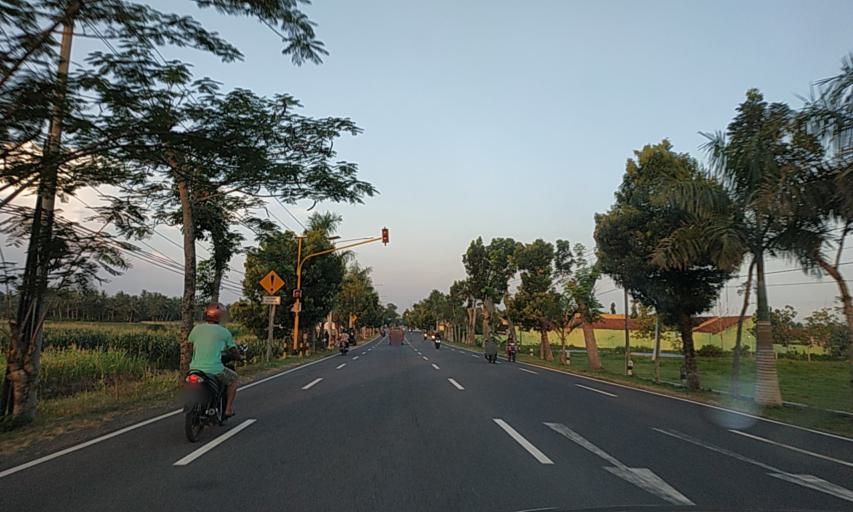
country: ID
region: Daerah Istimewa Yogyakarta
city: Srandakan
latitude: -7.8903
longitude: 110.1110
